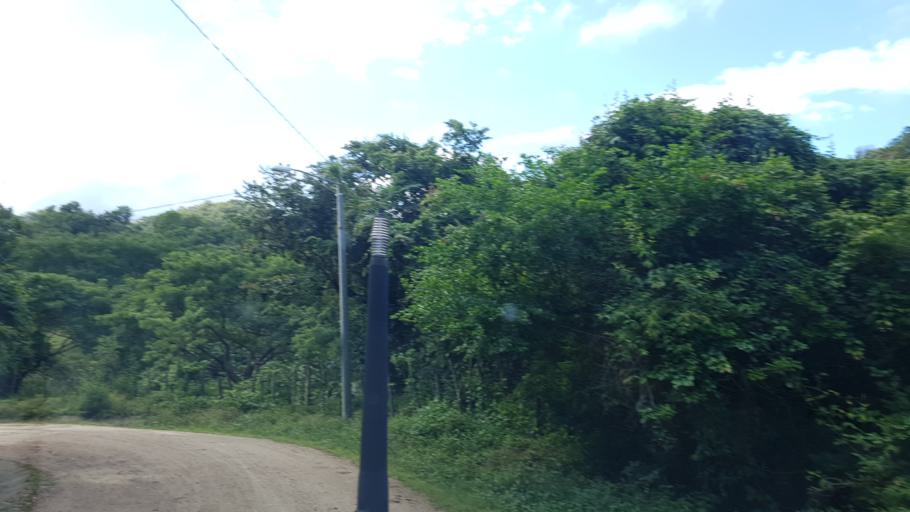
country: NI
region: Nueva Segovia
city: Ciudad Antigua
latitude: 13.6343
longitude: -86.3038
